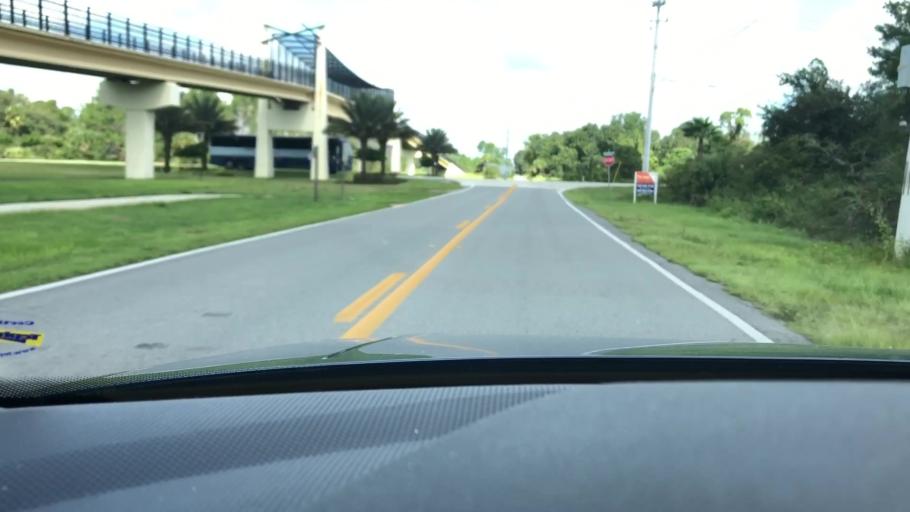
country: US
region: Florida
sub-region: Volusia County
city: Edgewater
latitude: 28.9503
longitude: -80.9451
